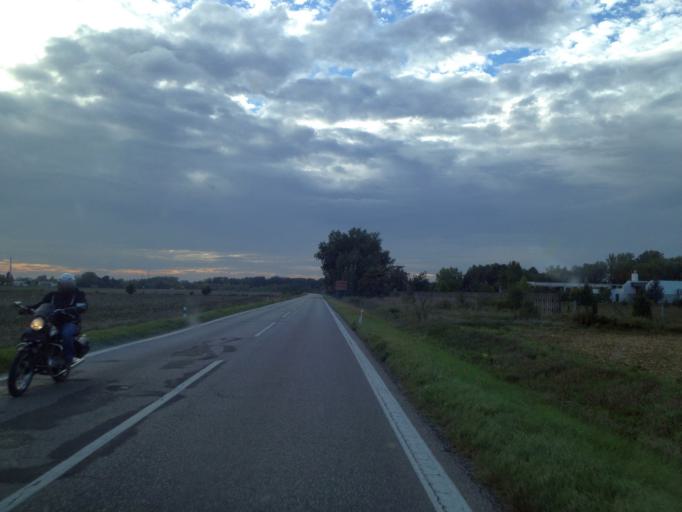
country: SK
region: Nitriansky
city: Komarno
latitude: 47.7654
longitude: 18.1651
